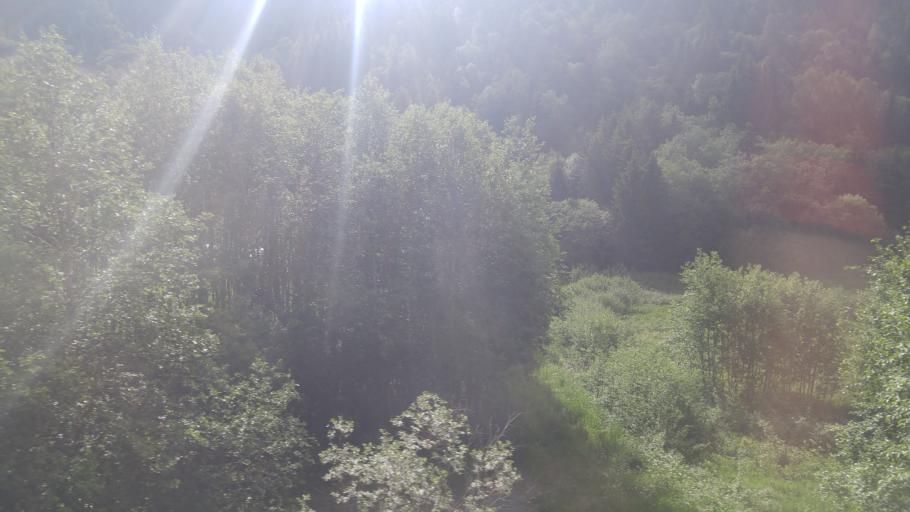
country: NO
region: Sor-Trondelag
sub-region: Melhus
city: Melhus
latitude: 63.2511
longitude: 10.2814
